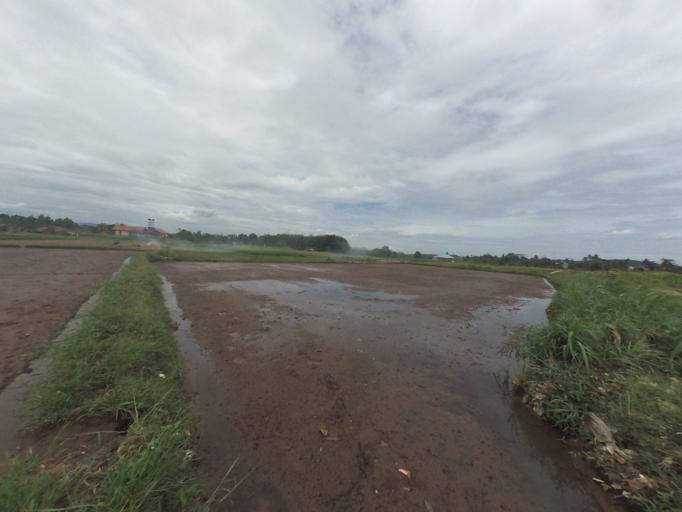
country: ID
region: West Java
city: Ciampea
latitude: -6.5505
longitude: 106.7399
